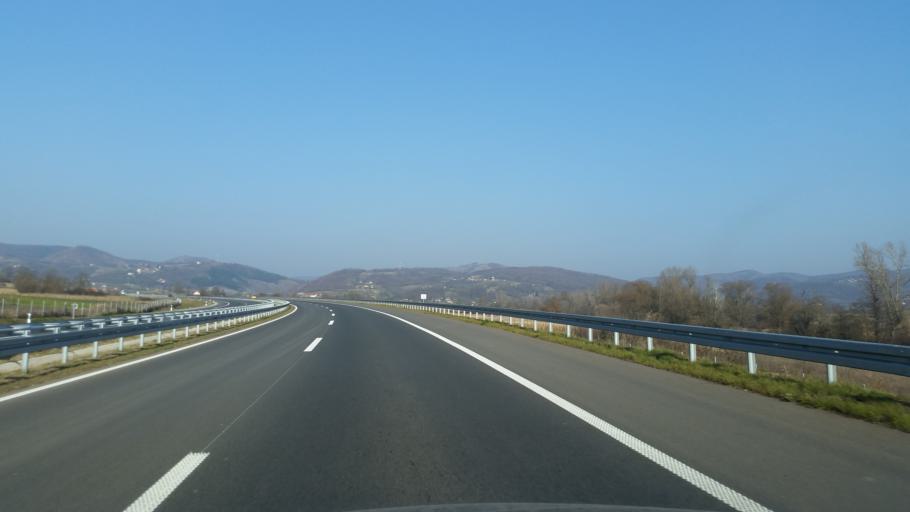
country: RS
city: Prislonica
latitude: 43.9500
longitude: 20.4009
